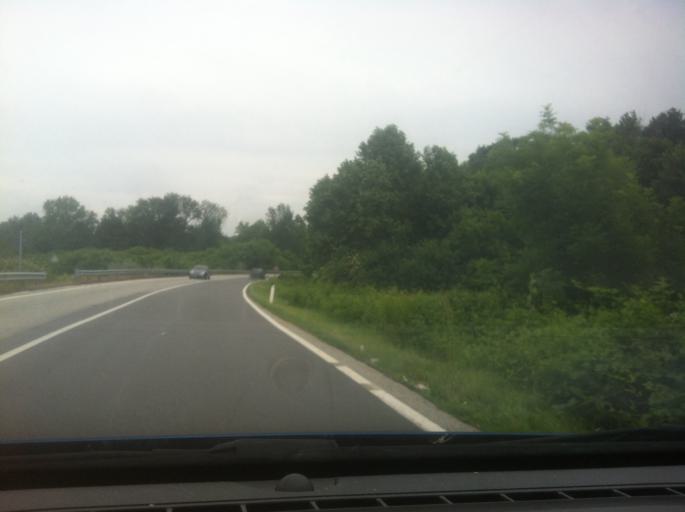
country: IT
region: Piedmont
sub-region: Provincia di Torino
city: San Benigno Canavese
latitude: 45.2422
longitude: 7.7990
